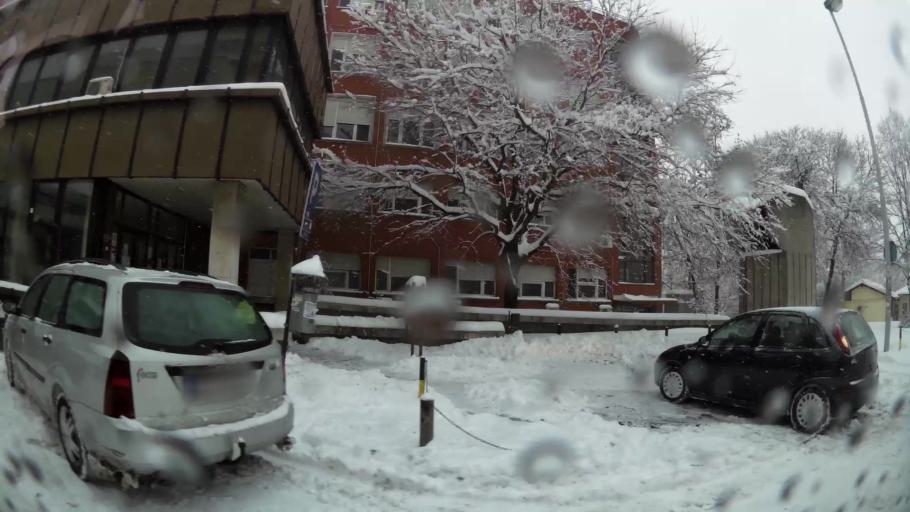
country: RS
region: Central Serbia
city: Belgrade
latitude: 44.7978
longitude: 20.4559
